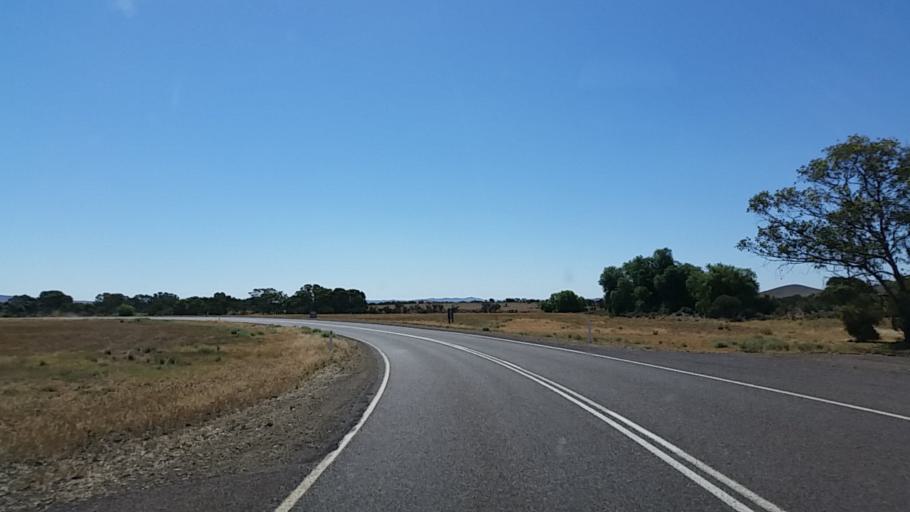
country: AU
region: South Australia
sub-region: Flinders Ranges
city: Quorn
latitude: -32.4224
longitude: 138.5301
